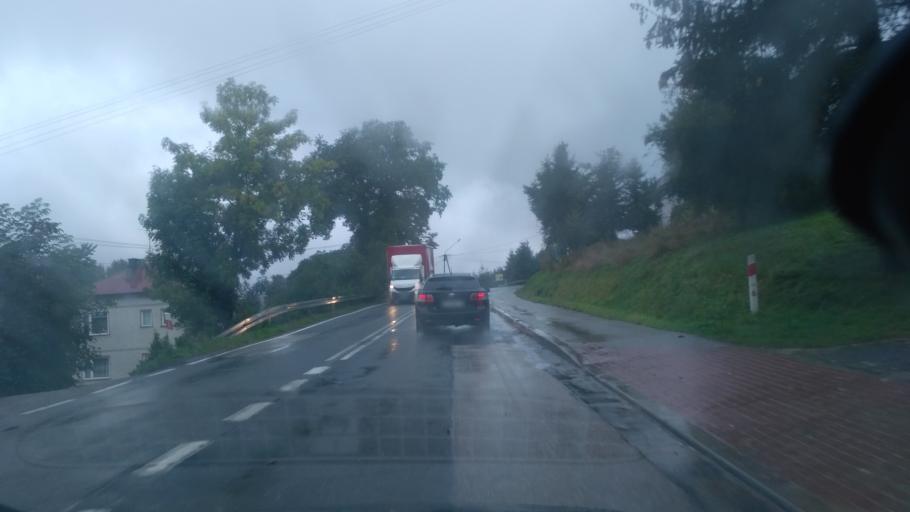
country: PL
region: Subcarpathian Voivodeship
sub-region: Powiat ropczycko-sedziszowski
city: Niedzwiada
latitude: 50.0117
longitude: 21.5523
